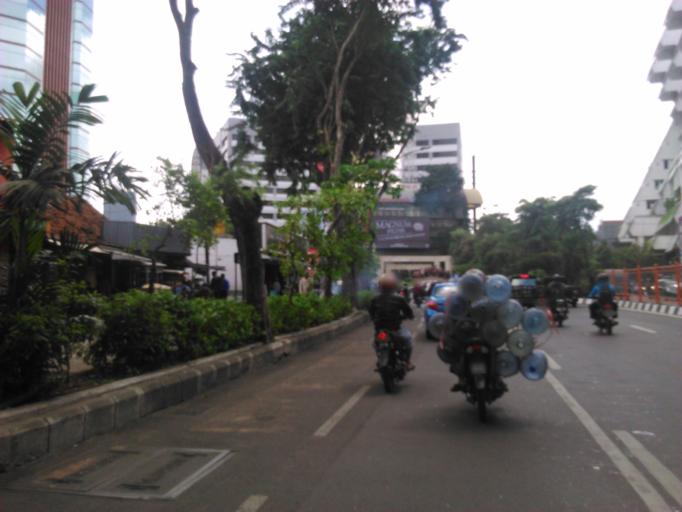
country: ID
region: East Java
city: Gubengairlangga
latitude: -7.2740
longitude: 112.7419
